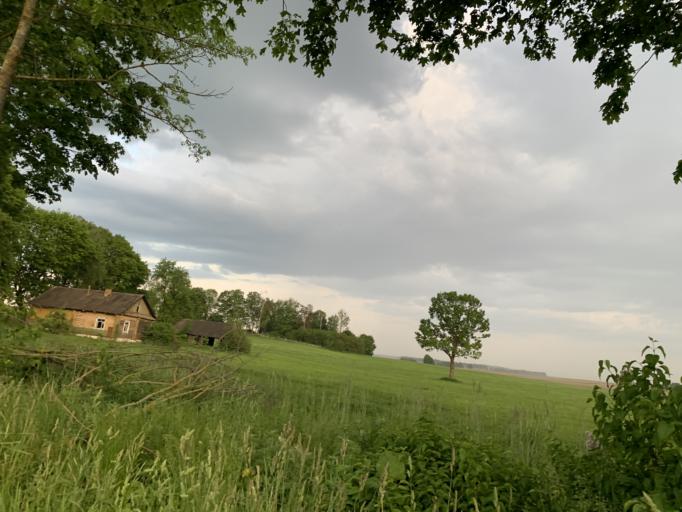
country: BY
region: Minsk
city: Nyasvizh
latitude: 53.1664
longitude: 26.8243
